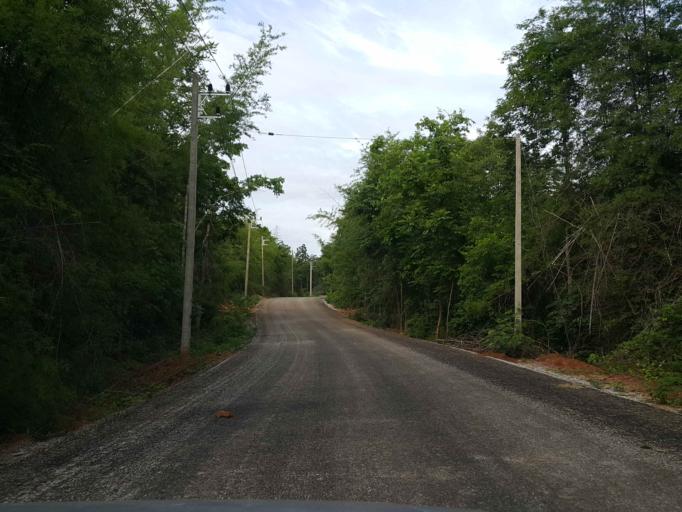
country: TH
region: Sukhothai
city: Thung Saliam
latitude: 17.2609
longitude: 99.5158
